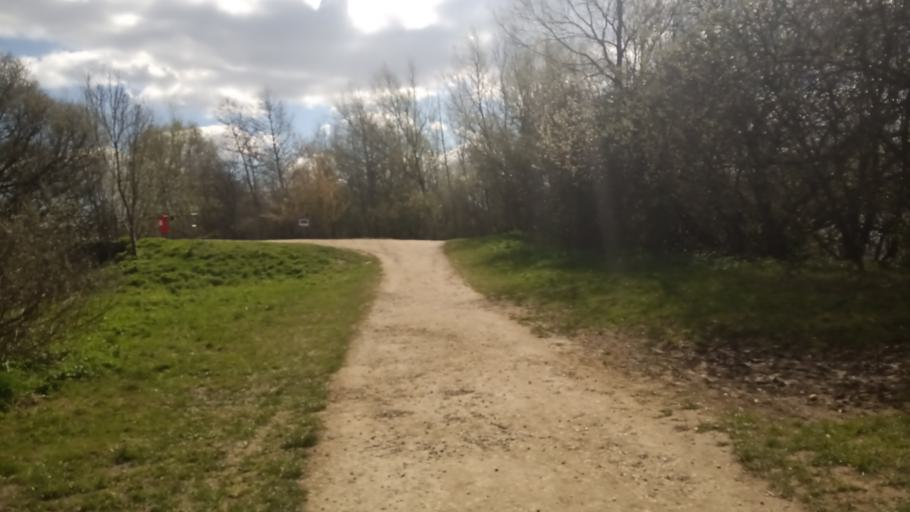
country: GB
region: England
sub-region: Oxfordshire
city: Ducklington
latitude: 51.7730
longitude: -1.4811
